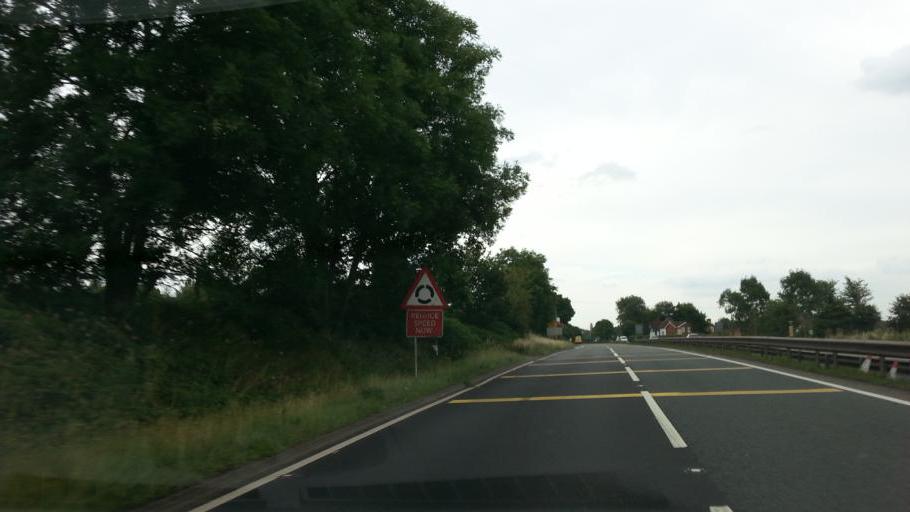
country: GB
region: England
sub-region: Herefordshire
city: Walford
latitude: 51.9140
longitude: -2.6073
